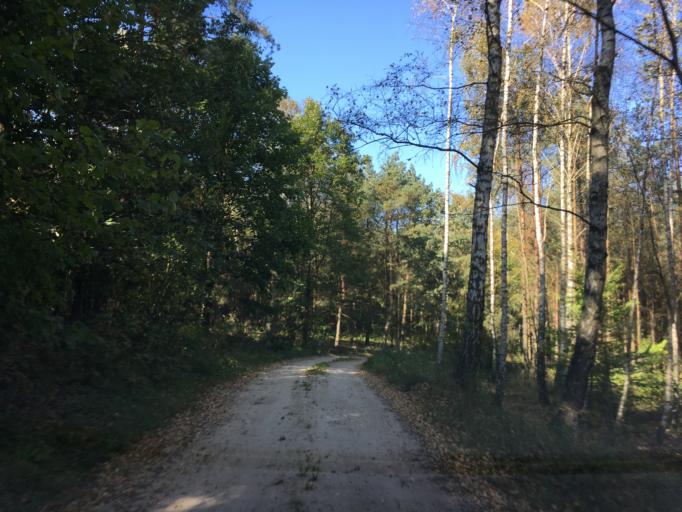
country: PL
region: Kujawsko-Pomorskie
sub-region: Powiat brodnicki
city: Bartniczka
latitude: 53.2655
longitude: 19.6723
